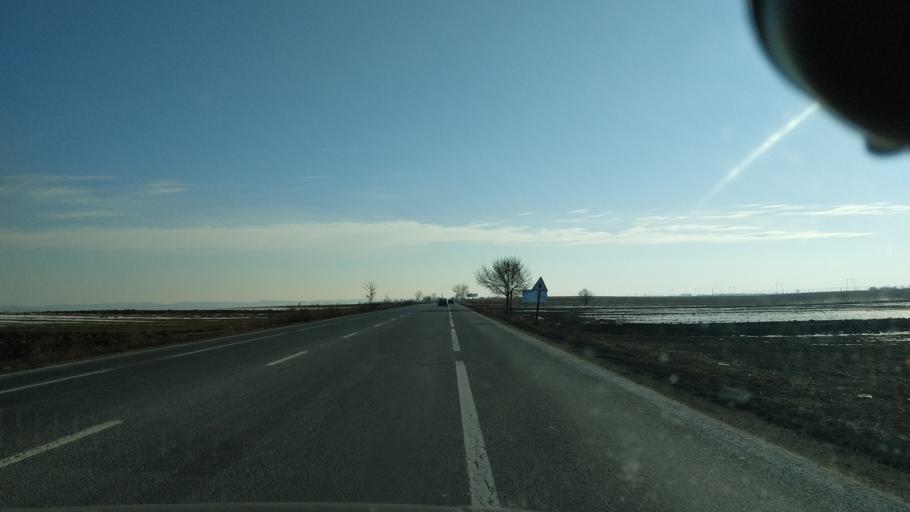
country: RO
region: Neamt
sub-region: Comuna Sabaoani
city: Traian
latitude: 47.0116
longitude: 26.8915
